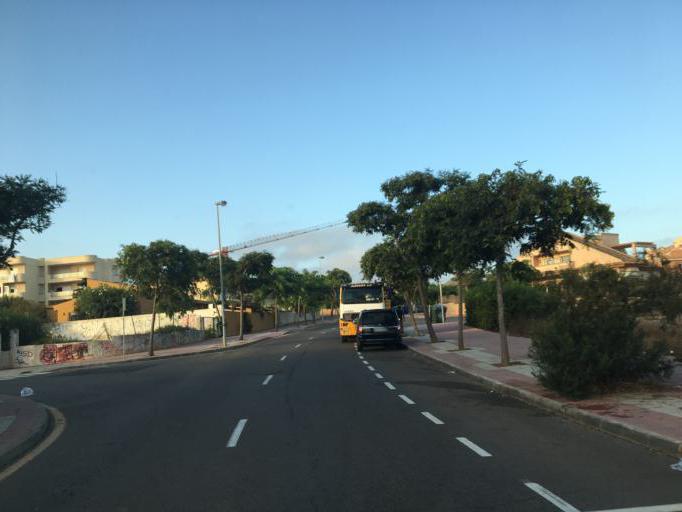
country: ES
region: Murcia
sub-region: Murcia
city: La Manga del Mar Menor
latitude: 37.6264
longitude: -0.7063
